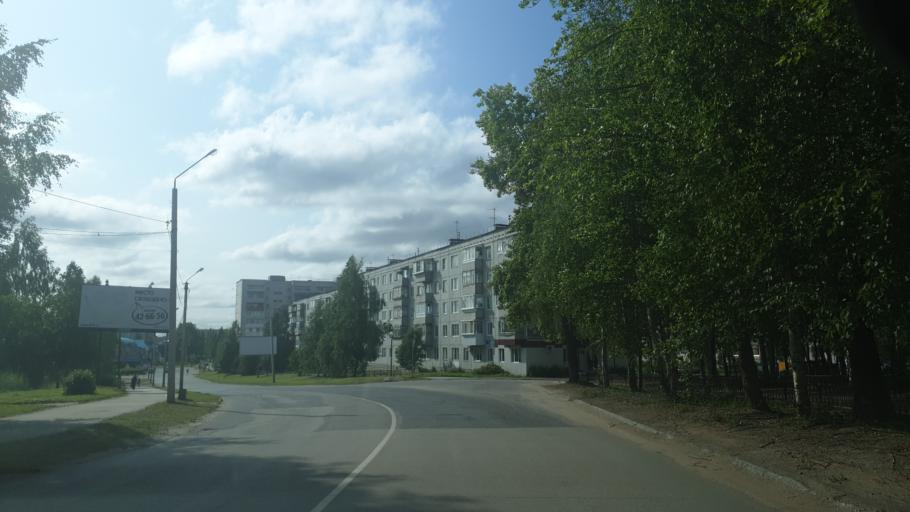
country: RU
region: Komi Republic
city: Ezhva
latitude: 61.7910
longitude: 50.7497
